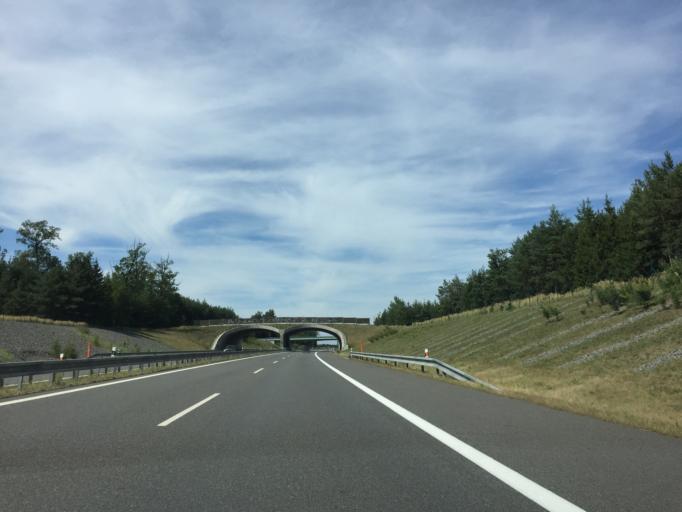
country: CZ
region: Jihocesky
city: Plana nad Luznici
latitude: 49.3548
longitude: 14.7255
